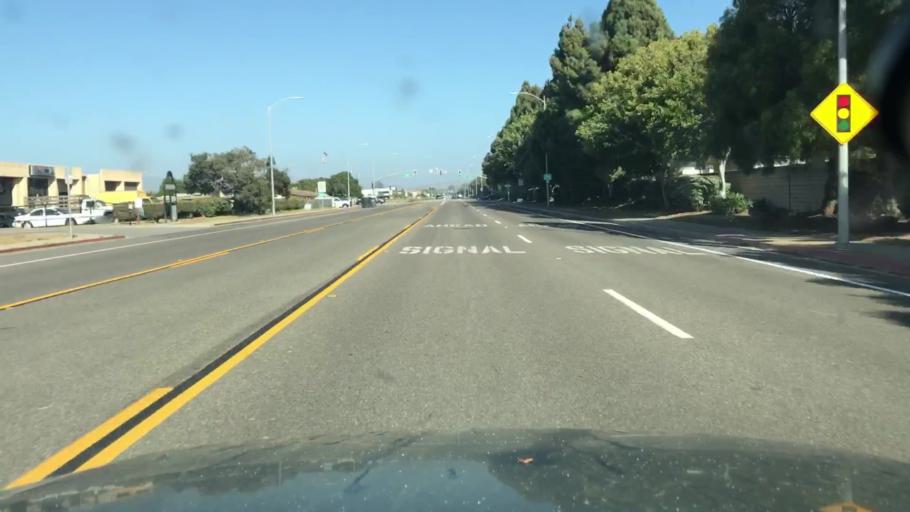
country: US
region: California
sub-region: Santa Barbara County
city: Lompoc
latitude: 34.6610
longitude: -120.4774
